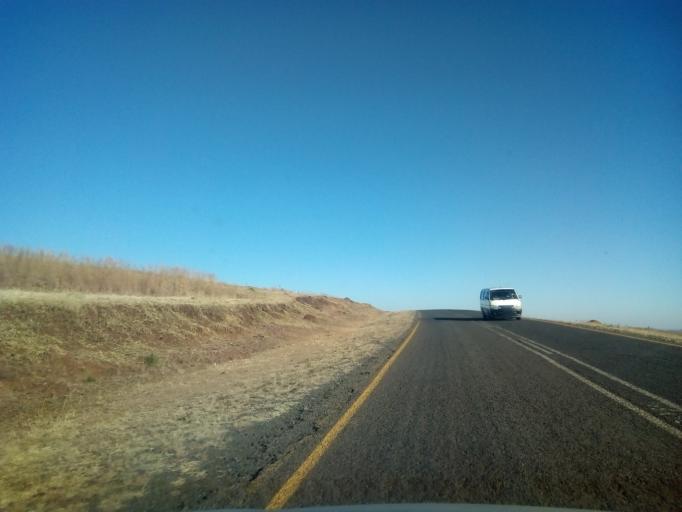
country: LS
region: Berea
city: Teyateyaneng
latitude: -29.2527
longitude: 27.7701
